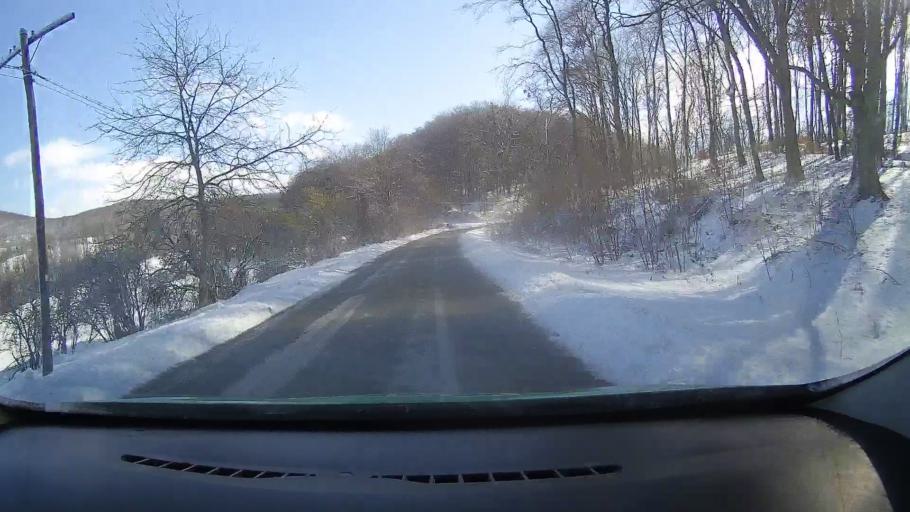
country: RO
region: Sibiu
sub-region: Comuna Mosna
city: Mosna
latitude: 46.0171
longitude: 24.4208
